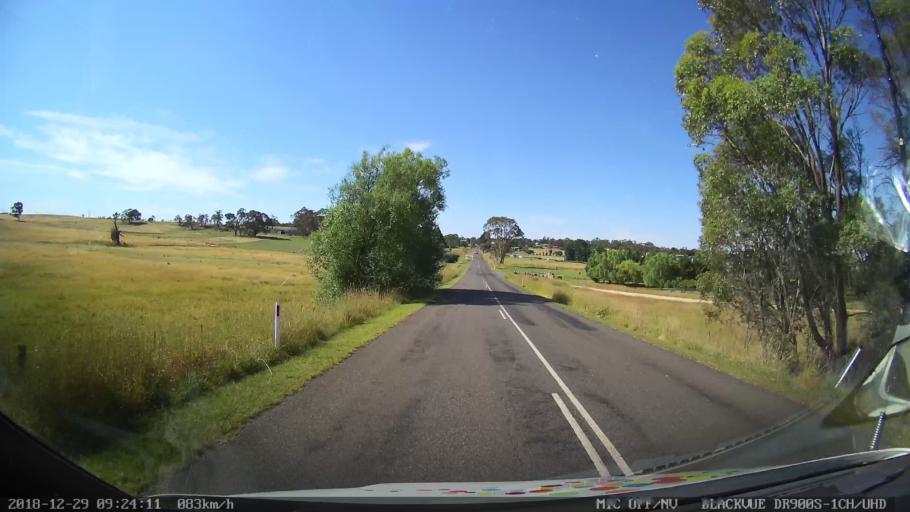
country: AU
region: New South Wales
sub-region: Upper Lachlan Shire
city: Crookwell
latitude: -34.5332
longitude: 149.3949
